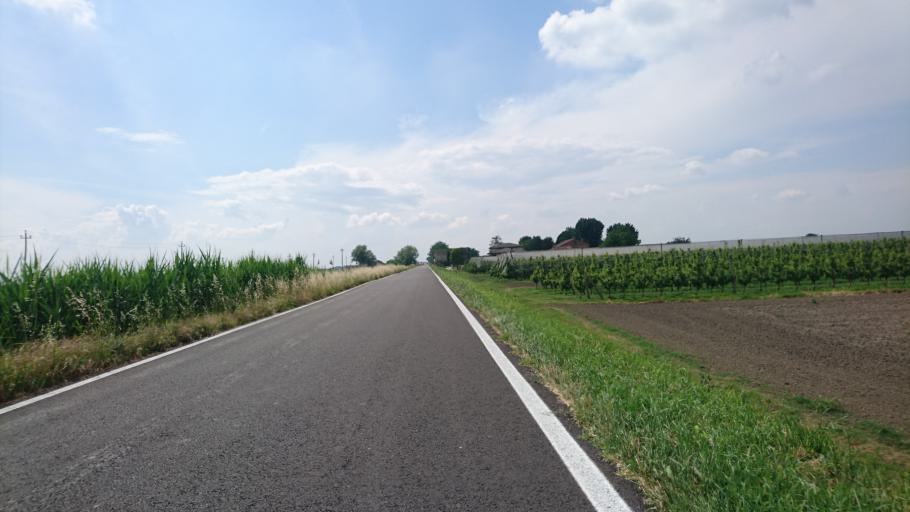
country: IT
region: Veneto
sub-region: Provincia di Verona
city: Castagnaro
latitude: 45.0720
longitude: 11.3902
